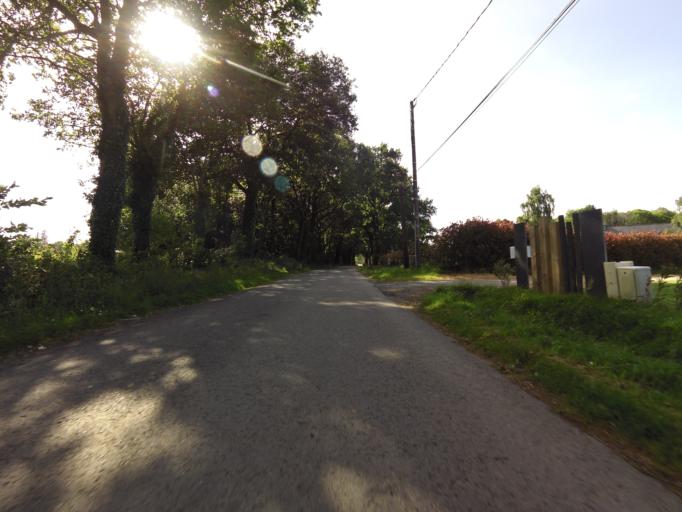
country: FR
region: Brittany
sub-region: Departement du Morbihan
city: Pluherlin
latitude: 47.7007
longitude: -2.3771
